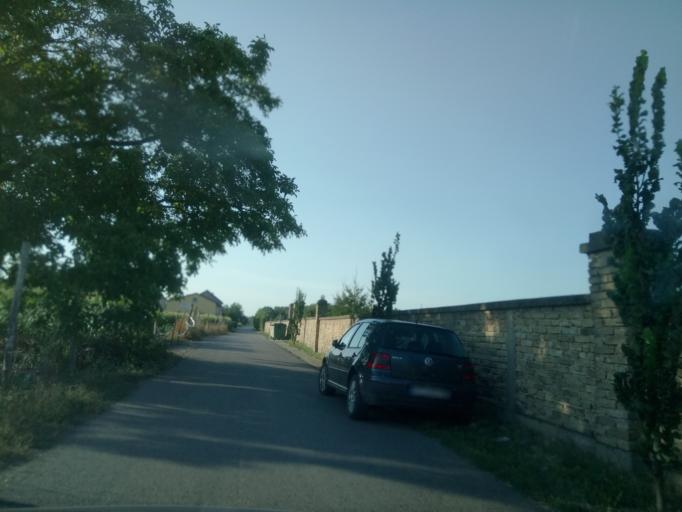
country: RS
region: Autonomna Pokrajina Vojvodina
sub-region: Sremski Okrug
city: Stara Pazova
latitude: 44.9929
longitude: 20.1624
